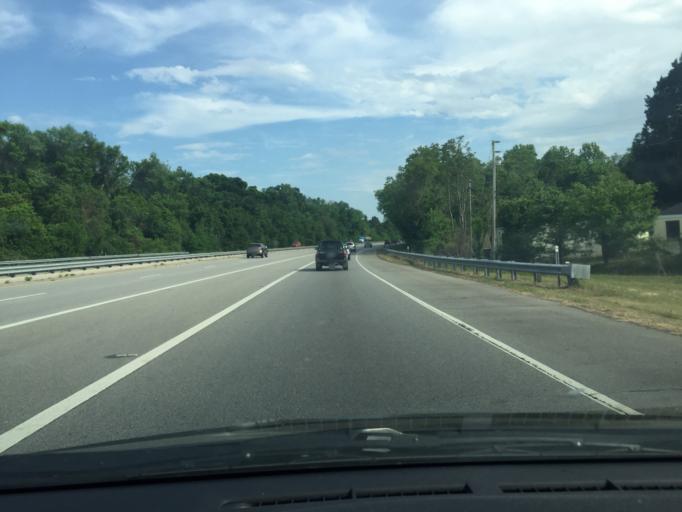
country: US
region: Georgia
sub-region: Chatham County
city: Thunderbolt
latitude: 32.0527
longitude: -81.0708
